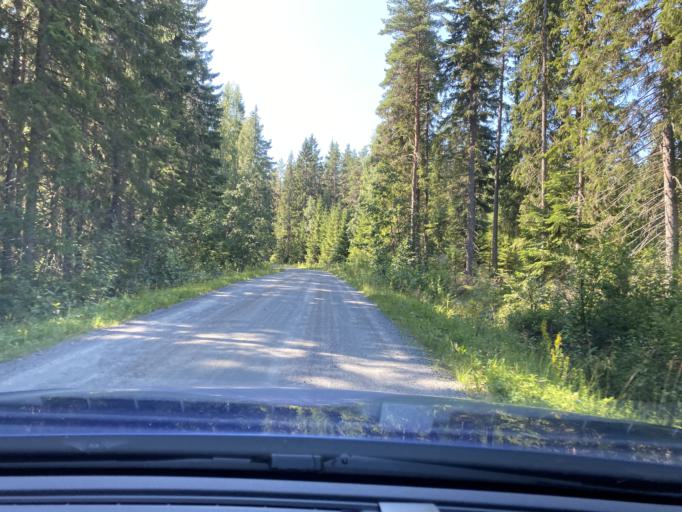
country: FI
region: Central Finland
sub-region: Jyvaeskylae
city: Korpilahti
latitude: 61.8689
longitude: 25.4004
